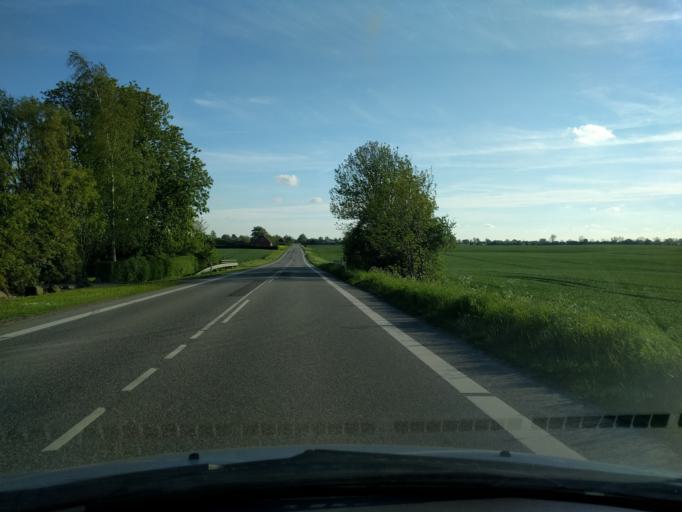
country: DK
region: Zealand
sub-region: Guldborgsund Kommune
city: Stubbekobing
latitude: 54.8459
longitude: 12.0095
